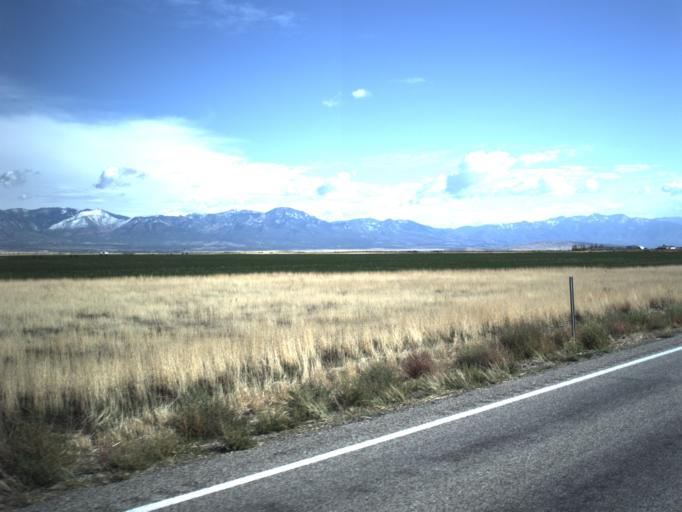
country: US
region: Utah
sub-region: Millard County
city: Delta
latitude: 39.1906
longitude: -112.4100
